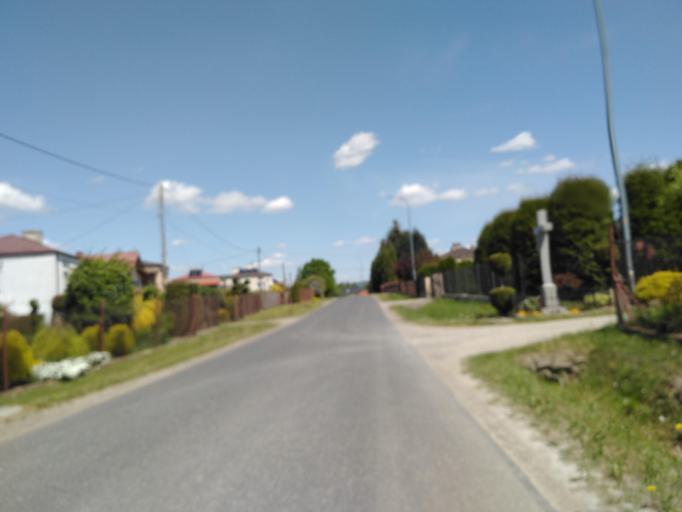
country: PL
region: Subcarpathian Voivodeship
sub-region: Powiat krosnienski
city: Jedlicze
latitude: 49.7030
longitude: 21.6869
